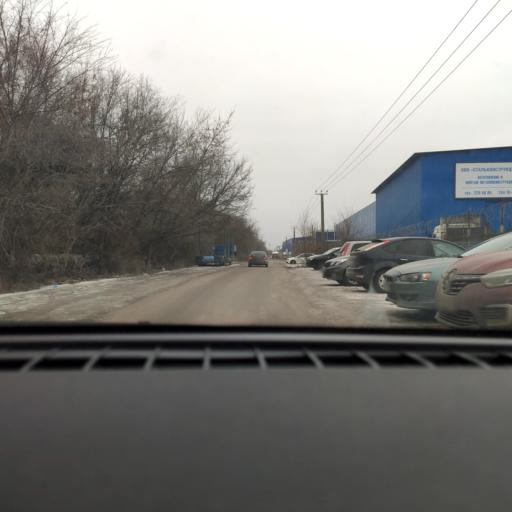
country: RU
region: Voronezj
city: Voronezh
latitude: 51.6500
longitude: 39.2649
